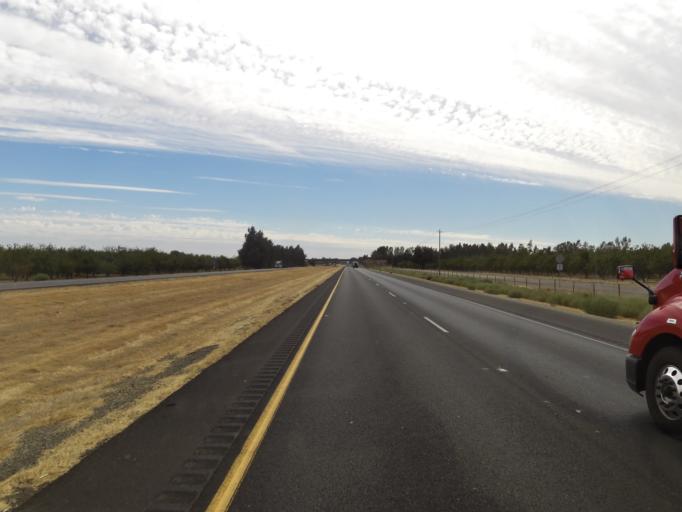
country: US
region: California
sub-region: Yolo County
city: Dunnigan
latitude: 38.9149
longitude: -121.9934
